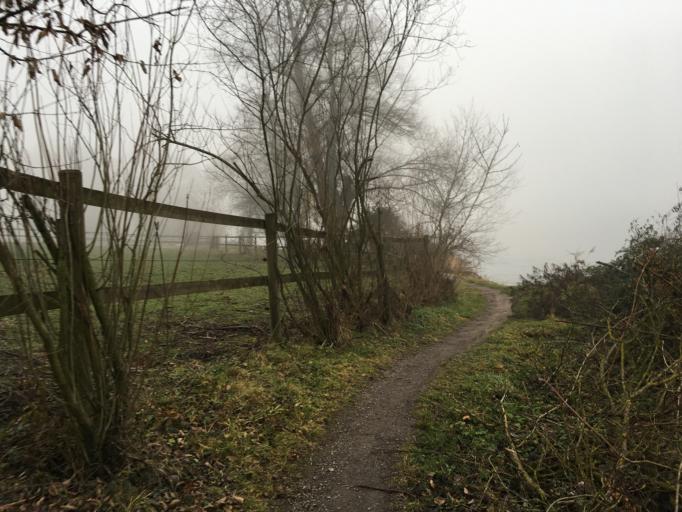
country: CH
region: Aargau
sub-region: Bezirk Zurzach
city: Koblenz
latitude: 47.6104
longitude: 8.2678
